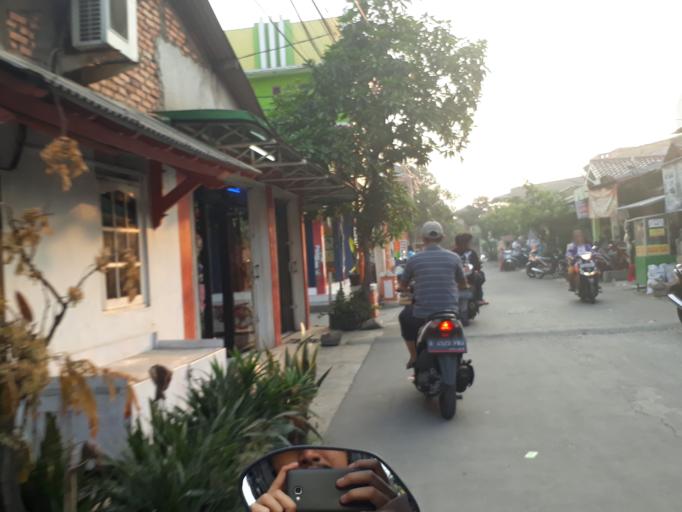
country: ID
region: West Java
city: Bekasi
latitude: -6.2433
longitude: 107.0524
